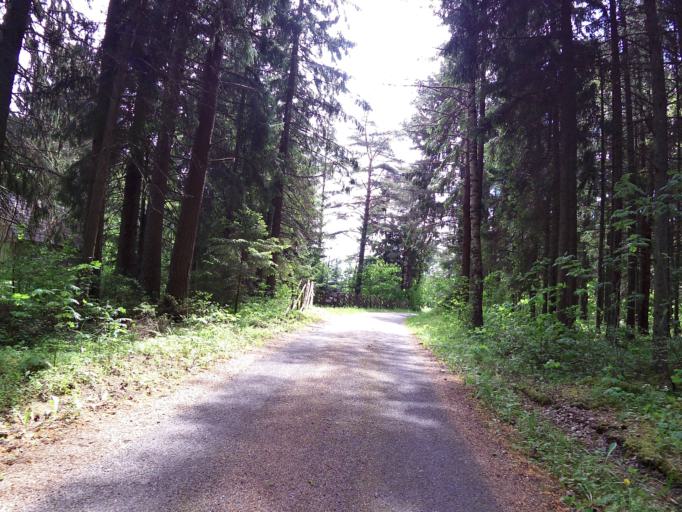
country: EE
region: Harju
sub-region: Paldiski linn
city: Paldiski
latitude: 59.2584
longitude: 23.7459
